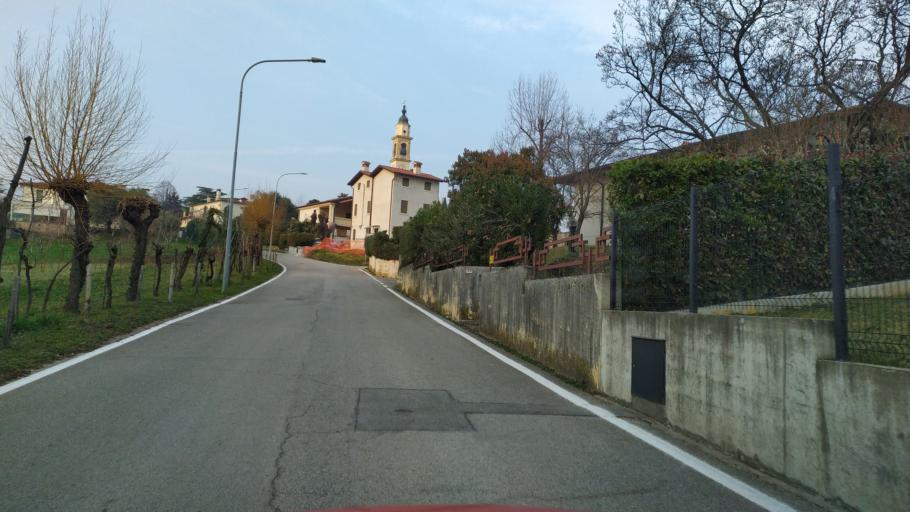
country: IT
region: Veneto
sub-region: Provincia di Vicenza
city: Sarcedo
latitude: 45.7055
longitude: 11.5260
